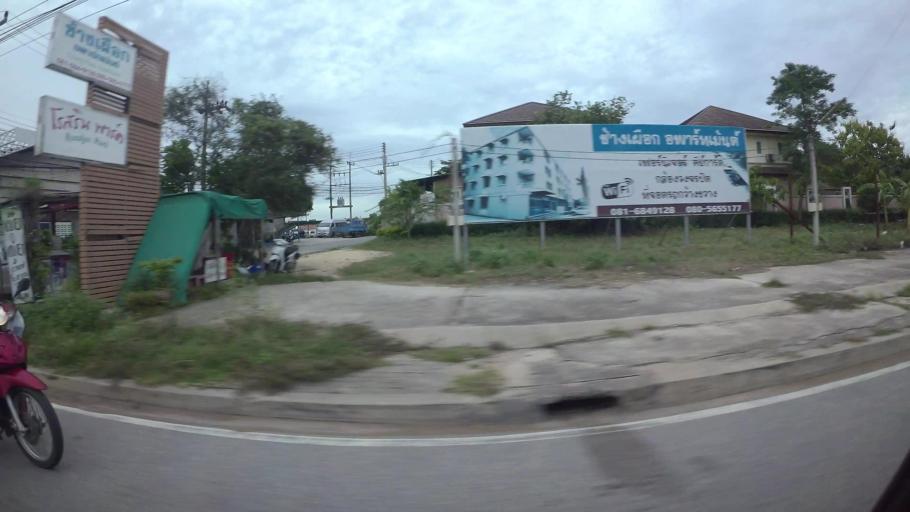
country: TH
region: Chon Buri
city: Si Racha
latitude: 13.1178
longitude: 100.9464
